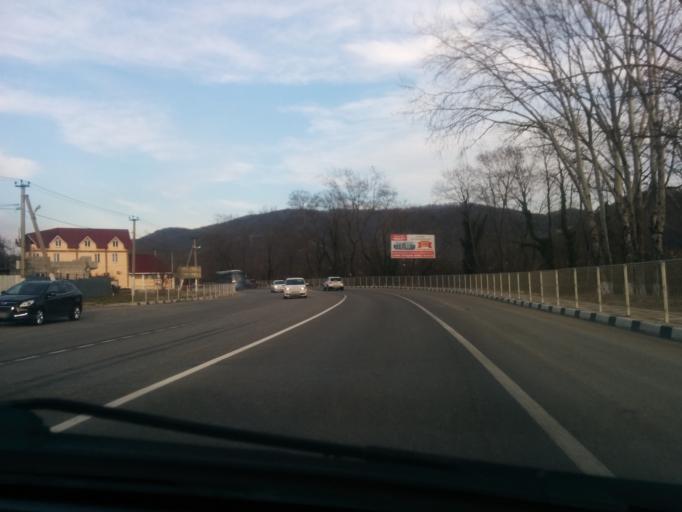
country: RU
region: Krasnodarskiy
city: Agoy
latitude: 44.1405
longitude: 39.0294
